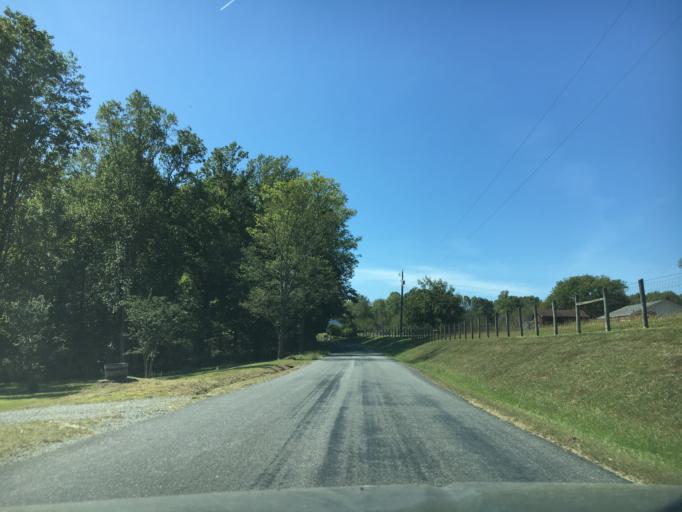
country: US
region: Virginia
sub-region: Albemarle County
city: Crozet
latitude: 38.0173
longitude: -78.7597
